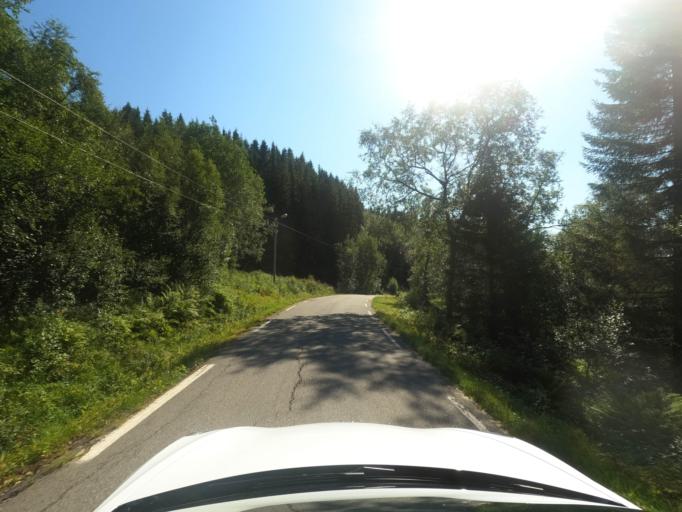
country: NO
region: Nordland
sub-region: Hadsel
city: Stokmarknes
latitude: 68.3061
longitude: 15.0927
